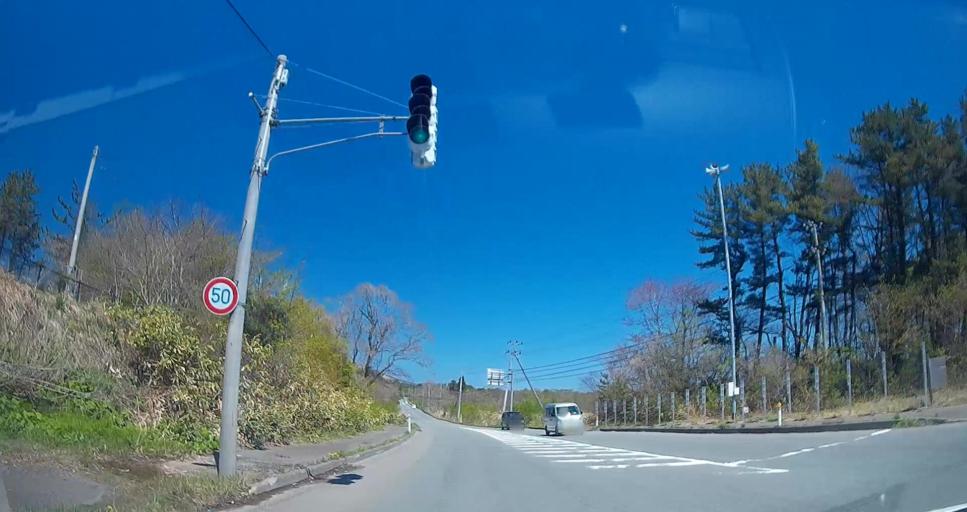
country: JP
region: Aomori
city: Misawa
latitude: 40.9906
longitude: 141.3679
